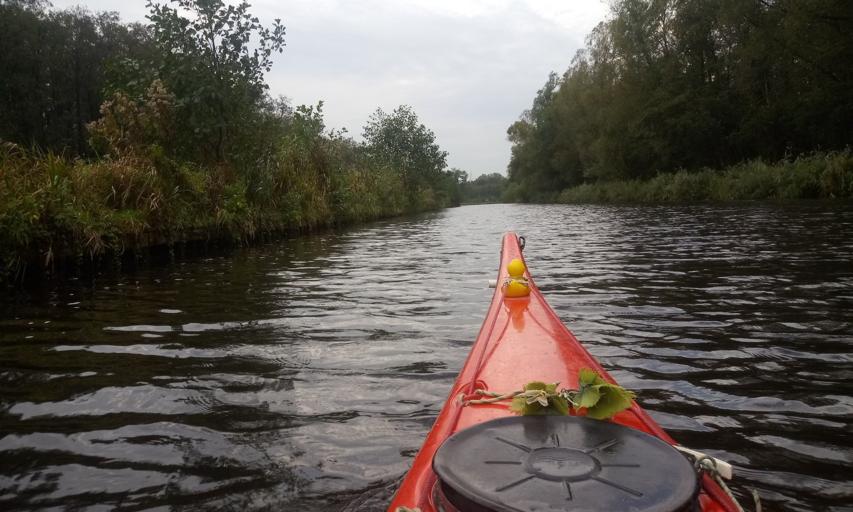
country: NL
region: North Holland
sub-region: Gemeente Wijdemeren
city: Oud-Loosdrecht
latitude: 52.2023
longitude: 5.1090
